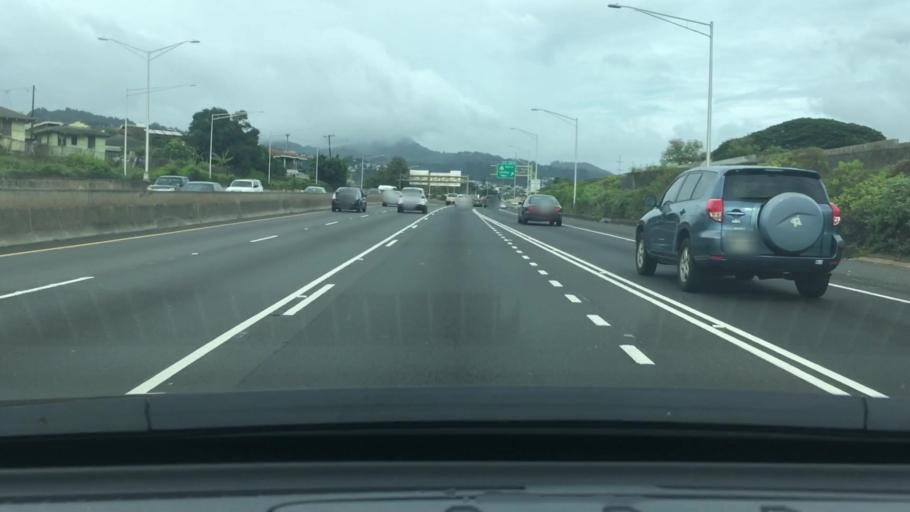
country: US
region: Hawaii
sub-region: Honolulu County
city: Honolulu
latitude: 21.3362
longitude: -157.8803
